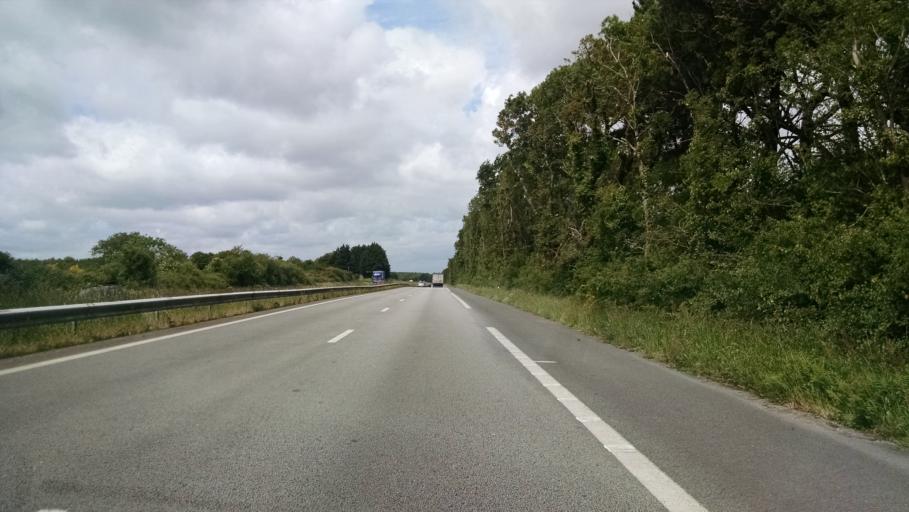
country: FR
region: Brittany
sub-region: Departement du Morbihan
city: Landaul
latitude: 47.7103
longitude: -3.0522
